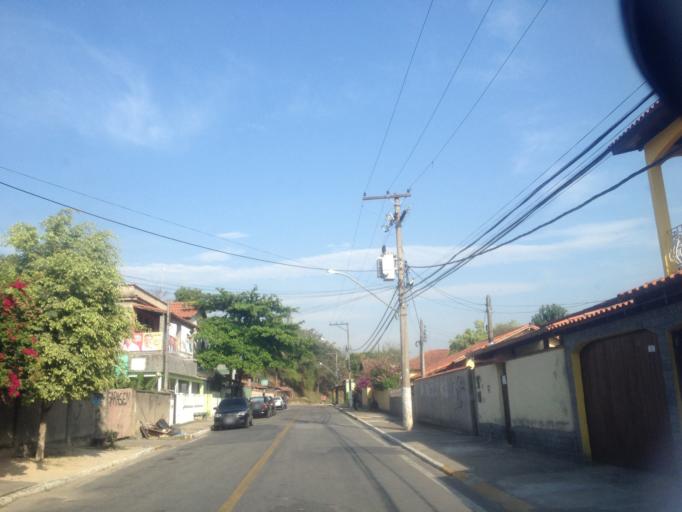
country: BR
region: Rio de Janeiro
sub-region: Porto Real
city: Porto Real
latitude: -22.4477
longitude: -44.3077
